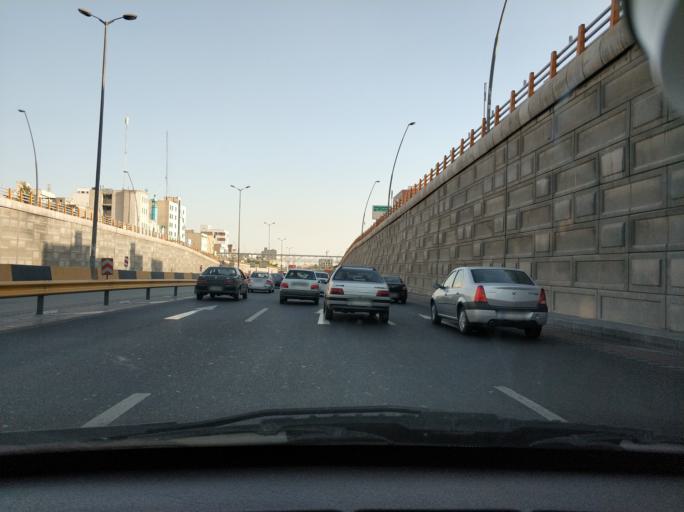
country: IR
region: Tehran
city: Tehran
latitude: 35.7007
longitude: 51.4572
